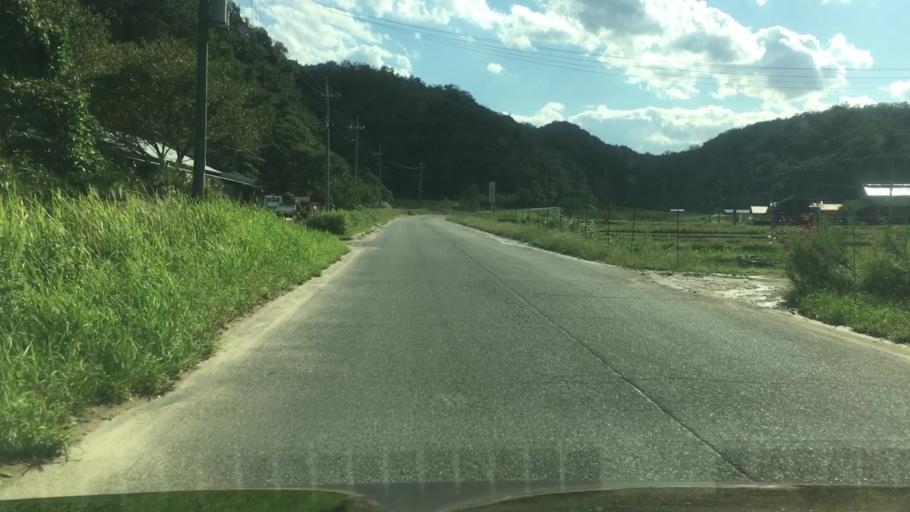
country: JP
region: Hyogo
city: Toyooka
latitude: 35.6478
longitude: 134.9649
